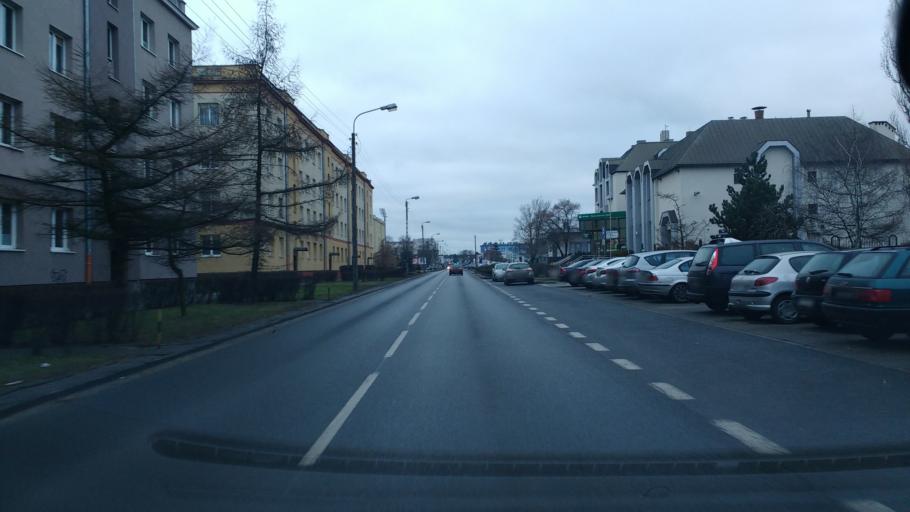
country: PL
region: Kujawsko-Pomorskie
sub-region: Bydgoszcz
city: Bydgoszcz
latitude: 53.1437
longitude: 18.0302
